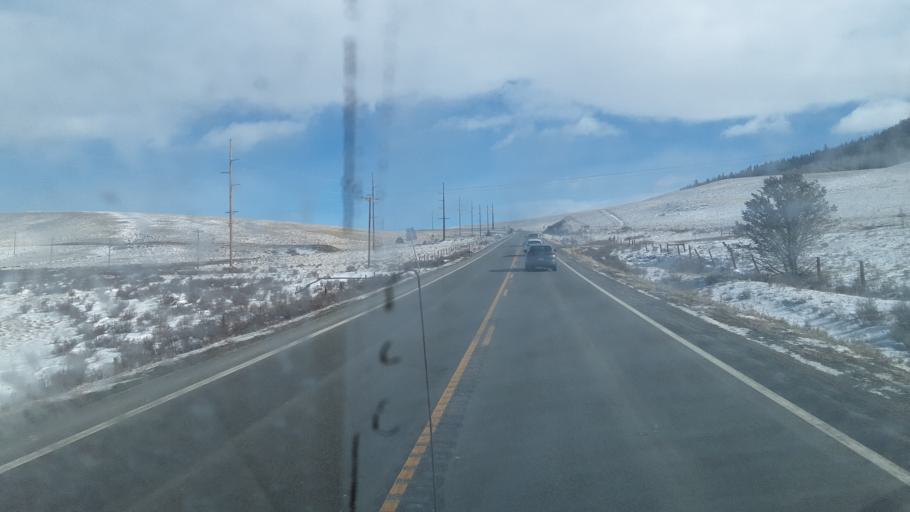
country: US
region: Colorado
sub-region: Park County
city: Fairplay
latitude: 39.2777
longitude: -105.9241
